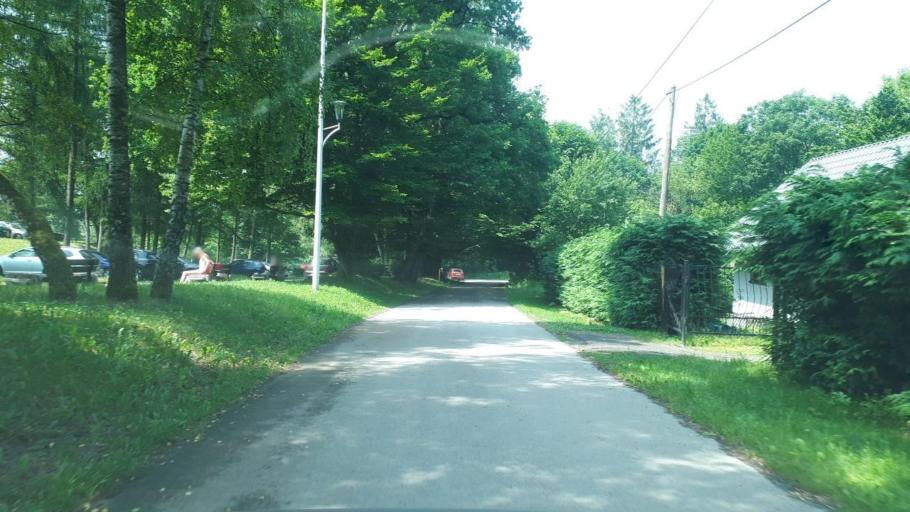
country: PL
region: Silesian Voivodeship
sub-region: Powiat cieszynski
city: Ustron
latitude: 49.7256
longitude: 18.8273
